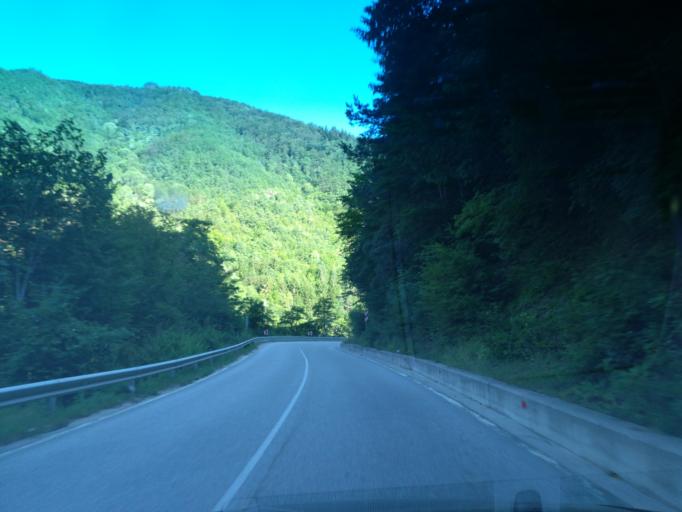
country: BG
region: Smolyan
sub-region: Obshtina Chepelare
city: Chepelare
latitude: 41.7957
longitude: 24.7098
